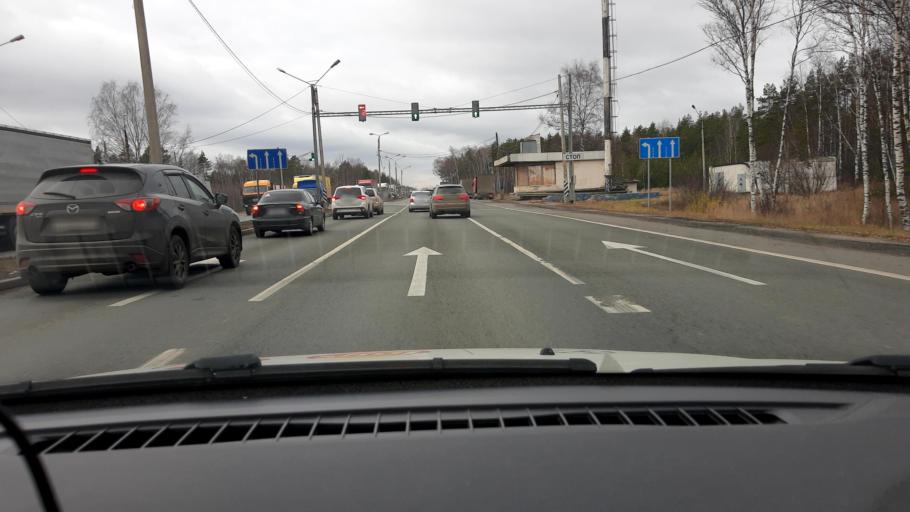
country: RU
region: Nizjnij Novgorod
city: Dzerzhinsk
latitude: 56.2987
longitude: 43.4777
